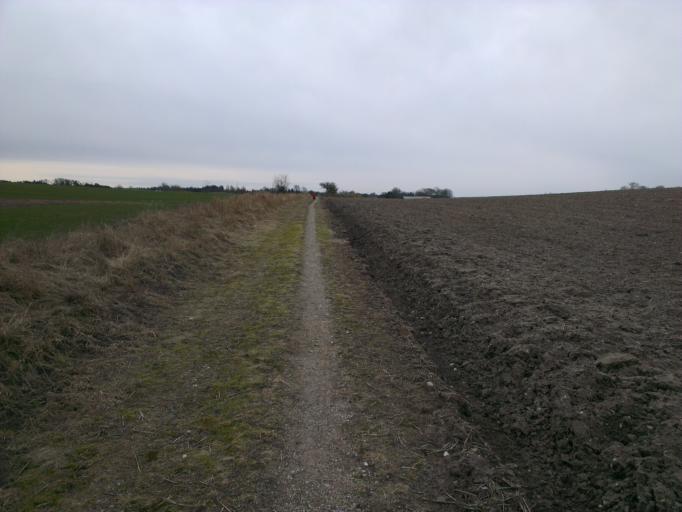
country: DK
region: Zealand
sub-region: Lejre Kommune
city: Ejby
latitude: 55.7650
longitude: 11.8749
